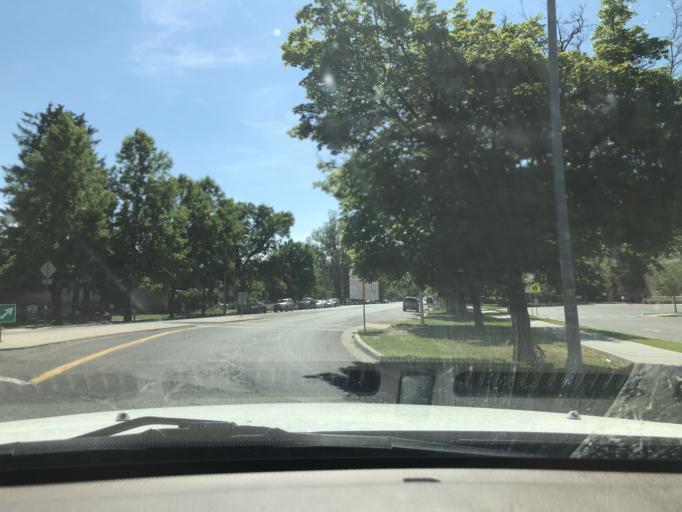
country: US
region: Utah
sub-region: Utah County
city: Provo
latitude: 40.2338
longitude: -111.6467
